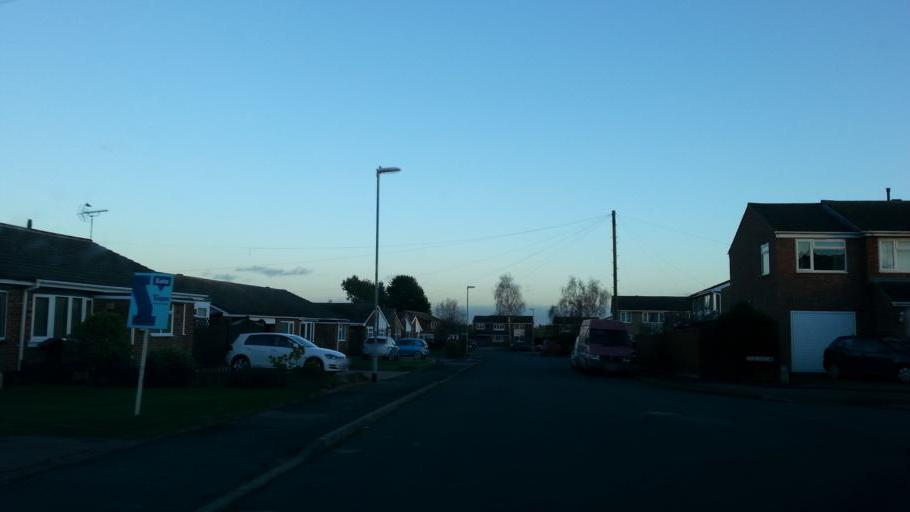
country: GB
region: England
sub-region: Cambridgeshire
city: Hemingford Grey
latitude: 52.2998
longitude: -0.0623
